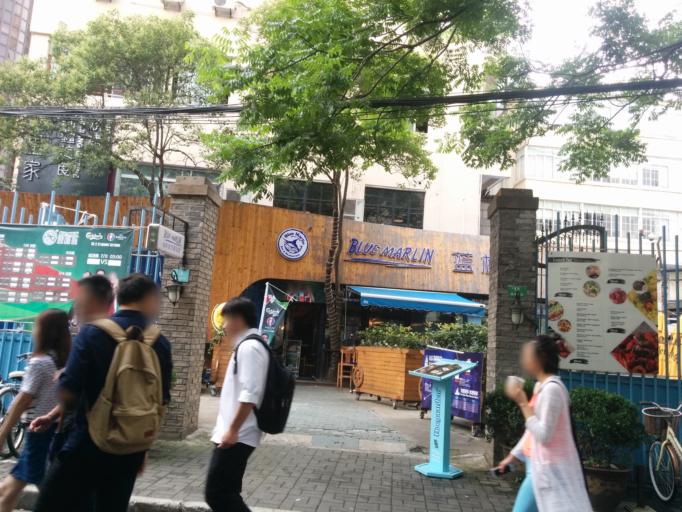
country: CN
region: Shanghai Shi
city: Shanghai
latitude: 31.2265
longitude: 121.4440
